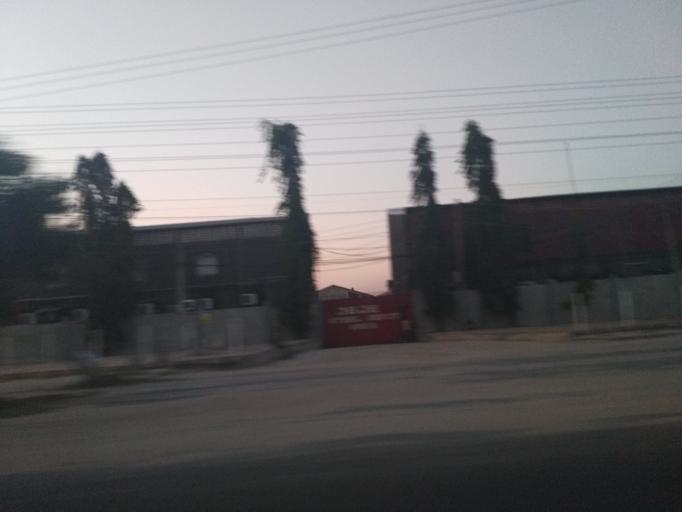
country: TZ
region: Dar es Salaam
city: Dar es Salaam
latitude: -6.8605
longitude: 39.2116
